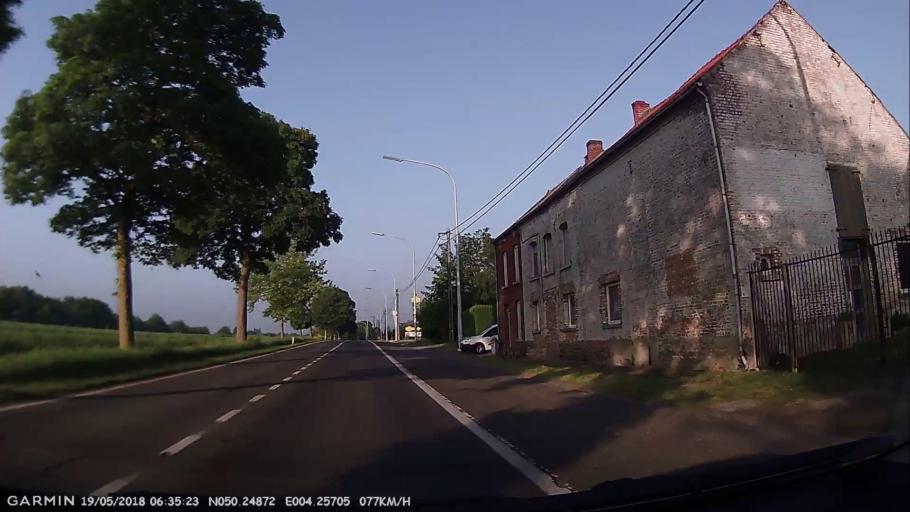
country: BE
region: Wallonia
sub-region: Province du Hainaut
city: Beaumont
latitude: 50.2486
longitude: 4.2569
